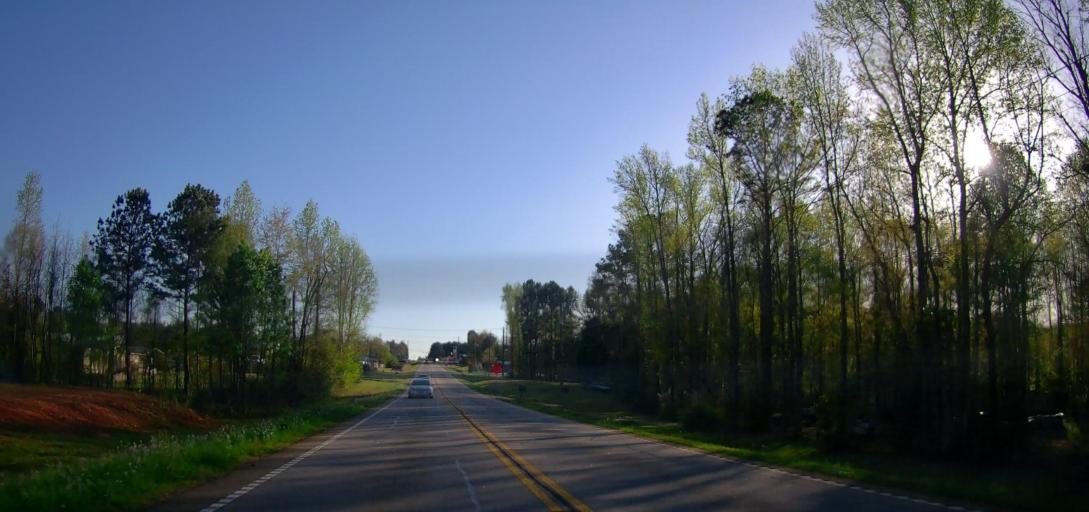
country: US
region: Georgia
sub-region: Butts County
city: Jackson
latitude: 33.3870
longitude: -83.9006
